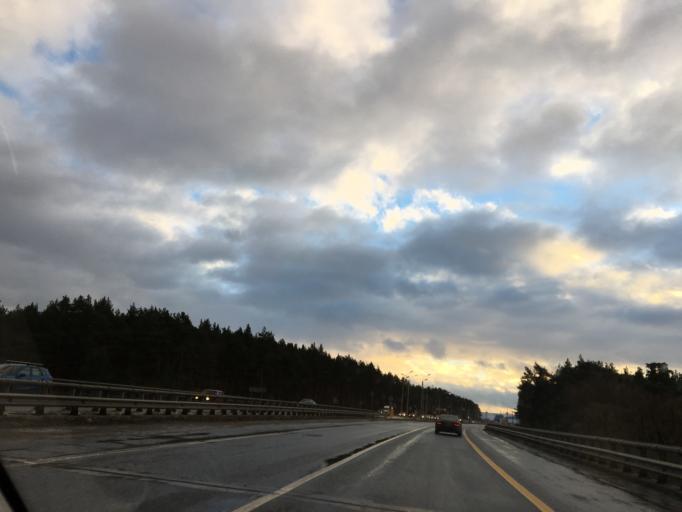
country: RU
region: Moskovskaya
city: Danki
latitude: 54.8861
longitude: 37.5116
